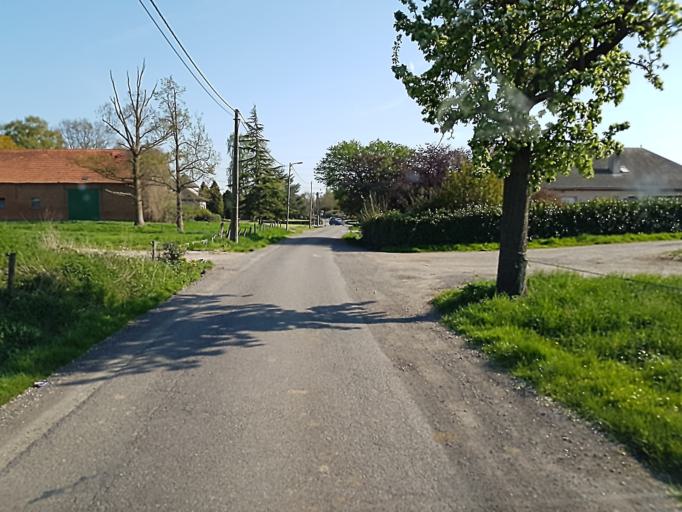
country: BE
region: Flanders
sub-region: Provincie Oost-Vlaanderen
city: Temse
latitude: 51.1426
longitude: 4.2185
